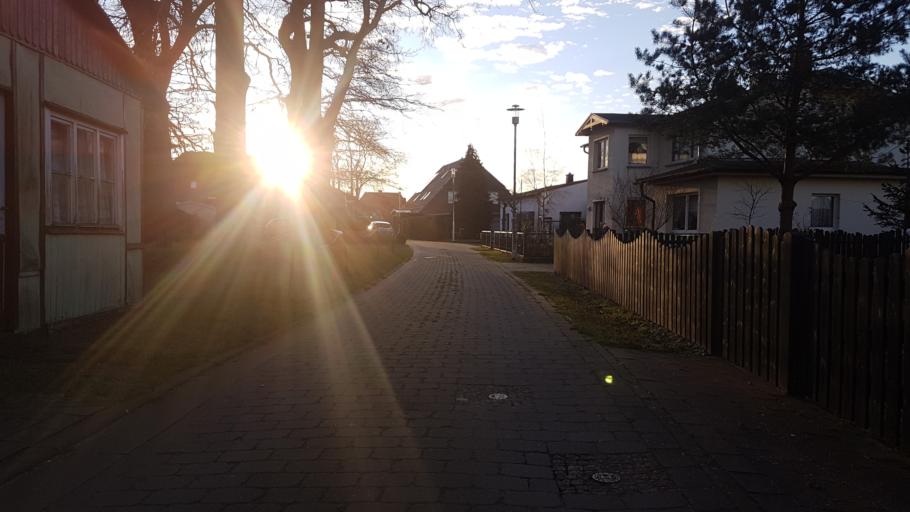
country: DE
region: Mecklenburg-Vorpommern
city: Ostseebad Sellin
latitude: 54.3587
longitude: 13.6997
